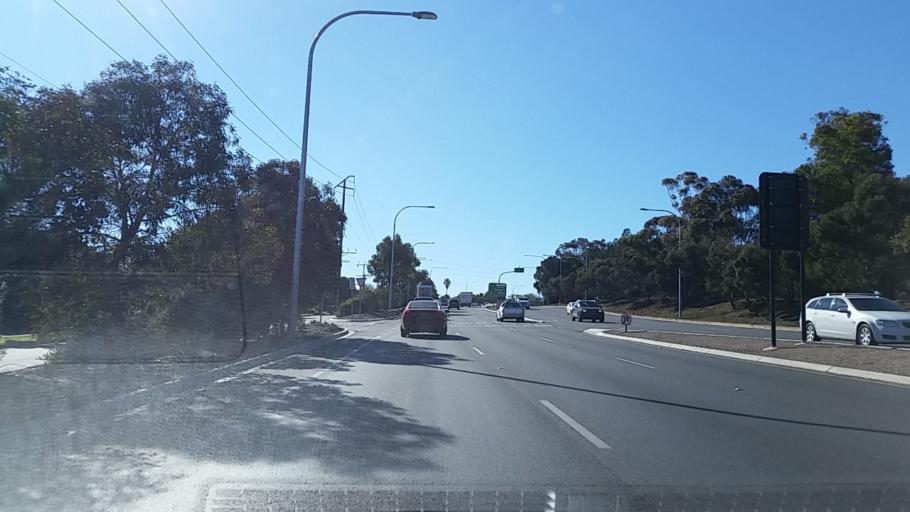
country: AU
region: South Australia
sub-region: Adelaide
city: North Adelaide
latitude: -34.9011
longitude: 138.5858
